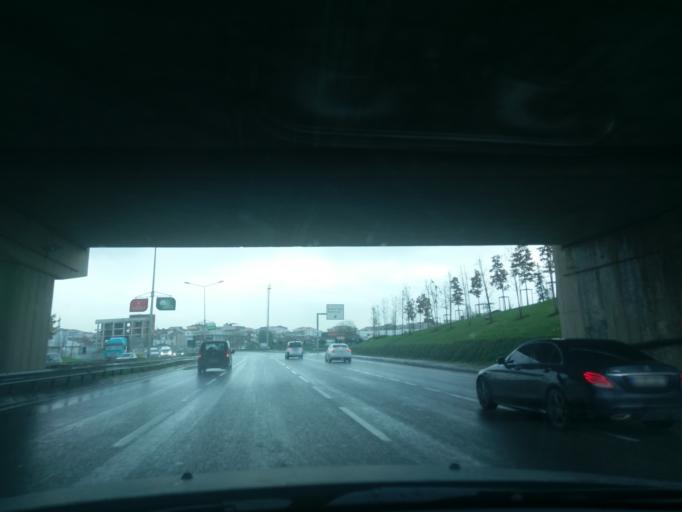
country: TR
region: Istanbul
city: Samandira
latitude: 41.0164
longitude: 29.1824
